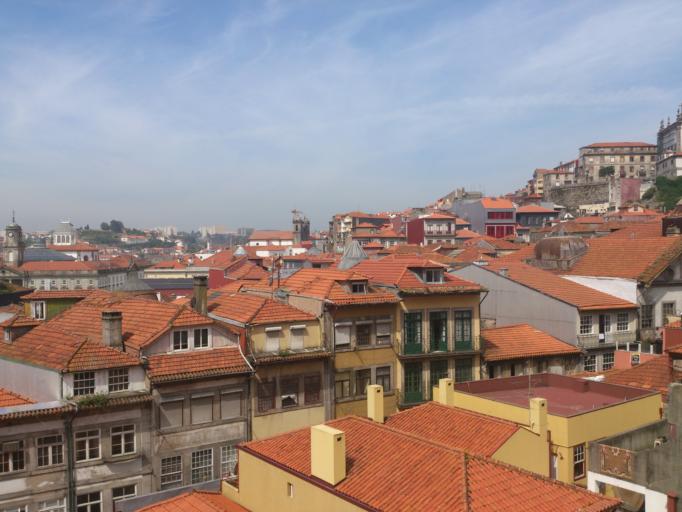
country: PT
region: Porto
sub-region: Porto
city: Porto
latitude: 41.1421
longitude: -8.6130
